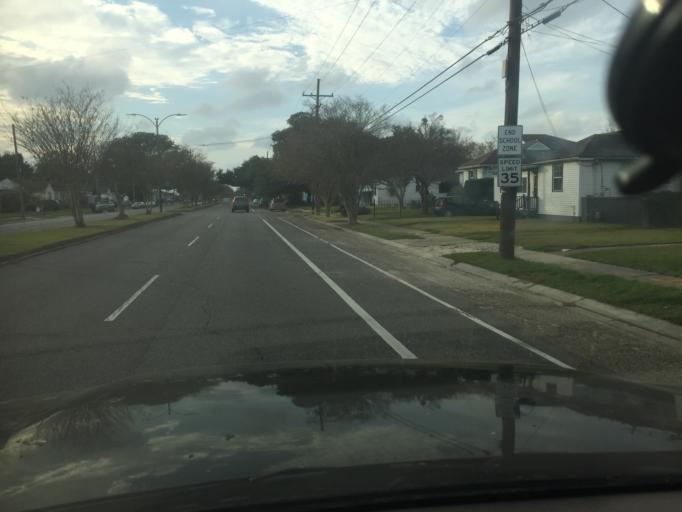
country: US
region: Louisiana
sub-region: Orleans Parish
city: New Orleans
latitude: 29.9888
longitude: -90.0765
